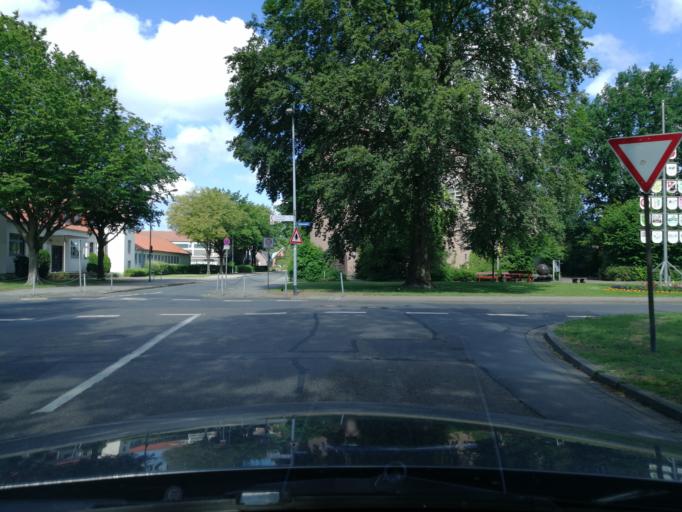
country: DE
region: North Rhine-Westphalia
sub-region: Regierungsbezirk Dusseldorf
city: Kleve
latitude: 51.7611
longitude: 6.0987
